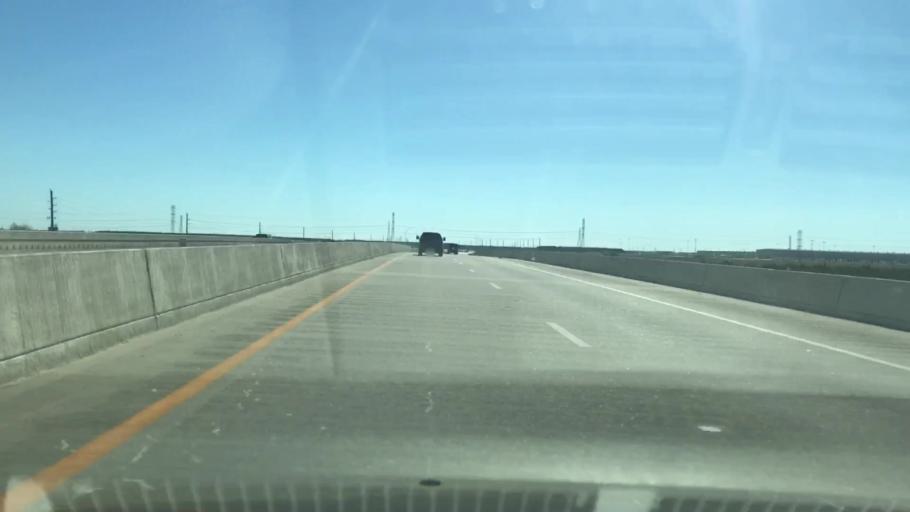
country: US
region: Texas
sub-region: Harris County
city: Cypress
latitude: 29.9225
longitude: -95.7623
